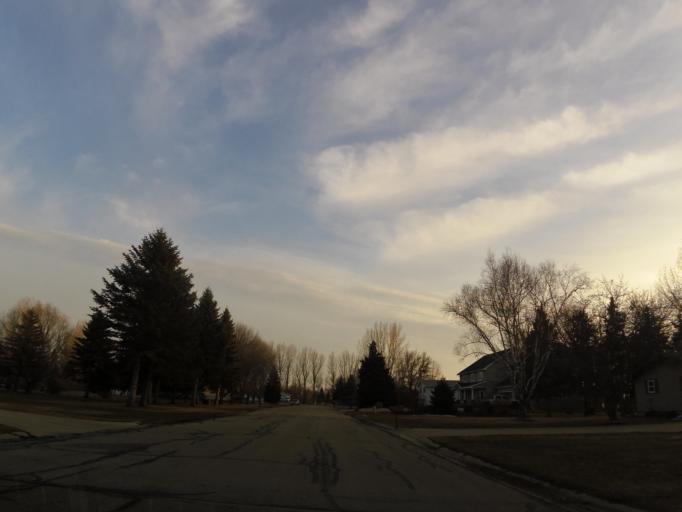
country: US
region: North Dakota
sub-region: Grand Forks County
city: Grand Forks
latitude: 47.8552
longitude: -97.0116
